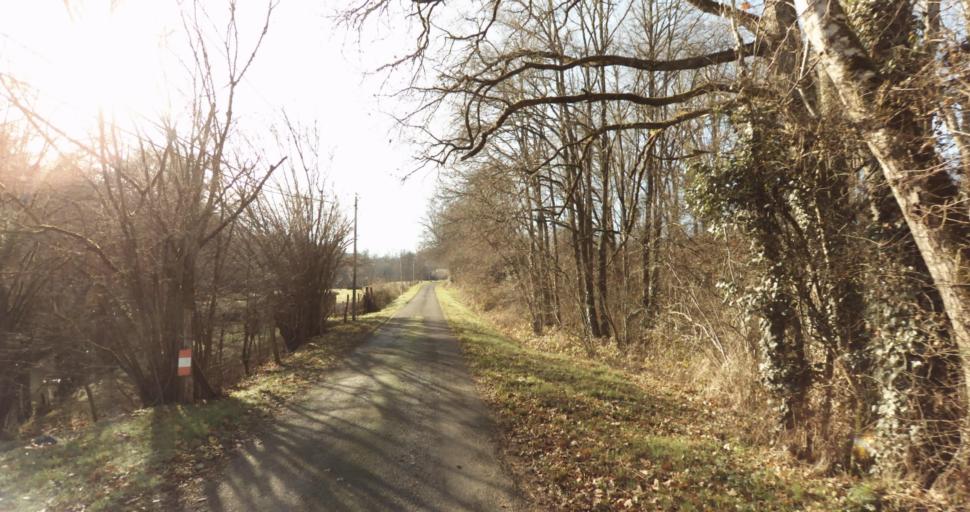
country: FR
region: Limousin
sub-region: Departement de la Haute-Vienne
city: Aixe-sur-Vienne
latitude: 45.7749
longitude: 1.1319
